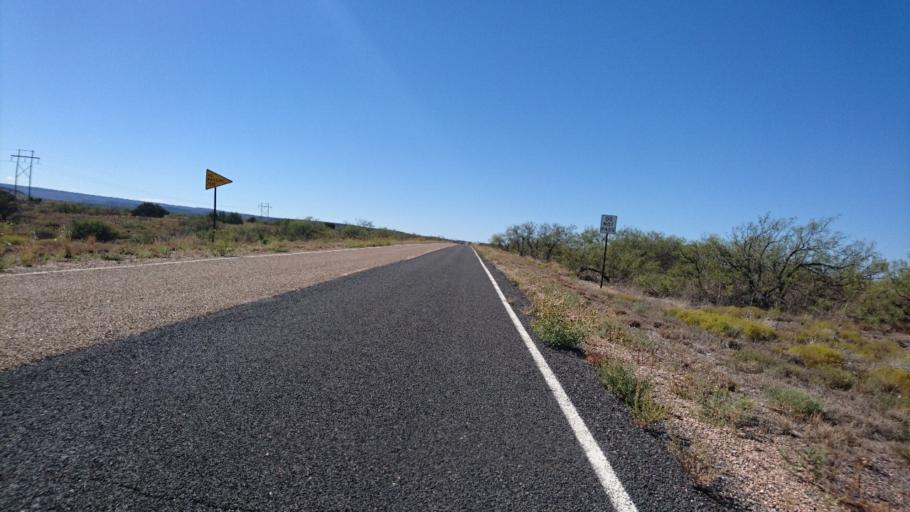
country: US
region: New Mexico
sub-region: Quay County
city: Tucumcari
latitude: 35.0779
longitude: -104.1311
